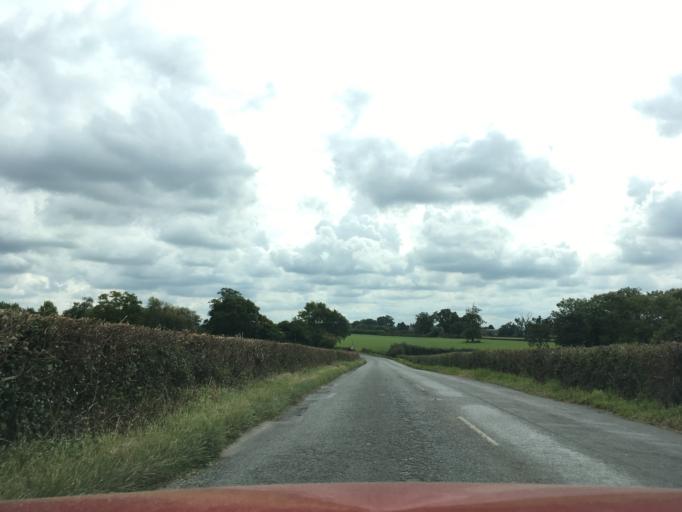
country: GB
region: England
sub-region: Gloucestershire
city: Berkeley
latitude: 51.6882
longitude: -2.4449
